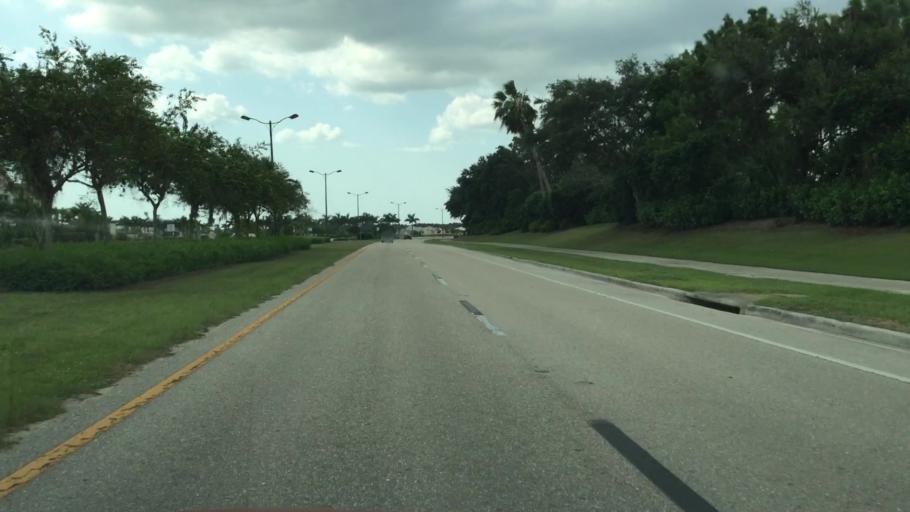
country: US
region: Florida
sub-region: Lee County
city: Estero
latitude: 26.4429
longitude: -81.7727
